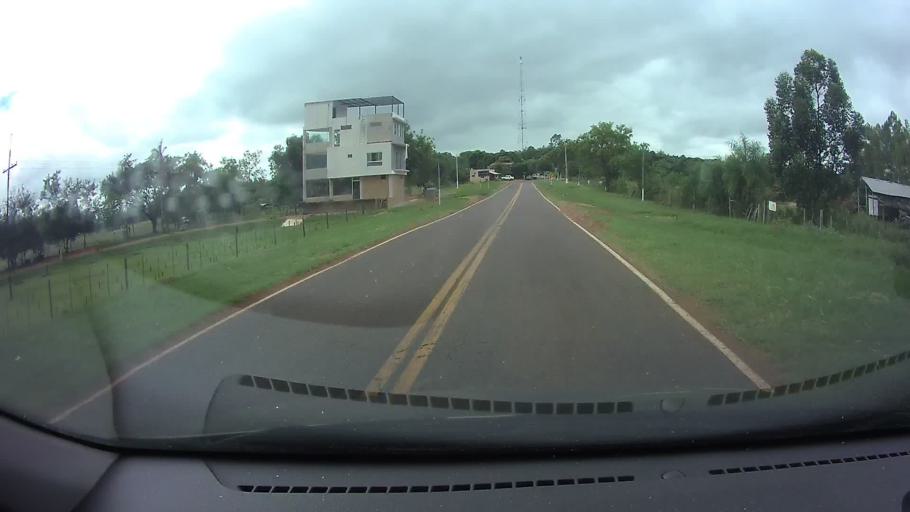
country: PY
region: Paraguari
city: Acahay
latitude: -25.9052
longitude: -57.1152
